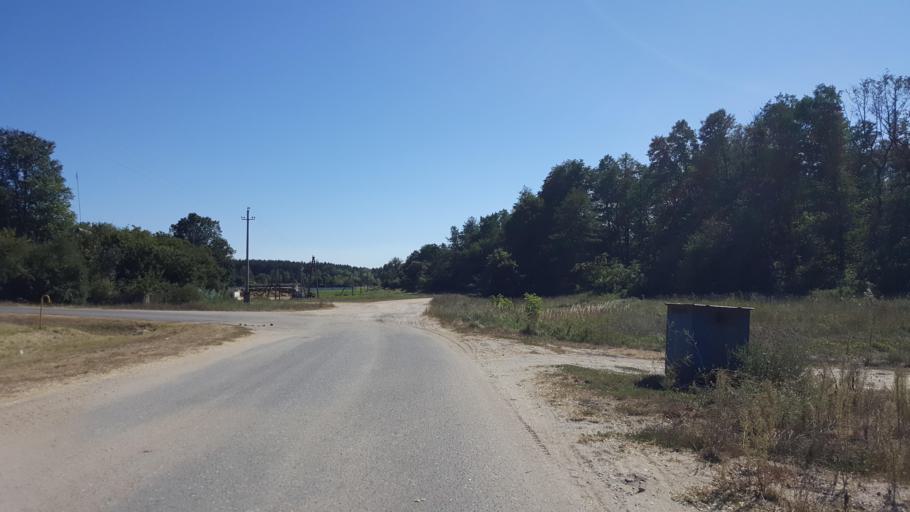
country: PL
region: Lublin Voivodeship
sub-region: Powiat bialski
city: Rokitno
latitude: 52.2264
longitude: 23.3453
